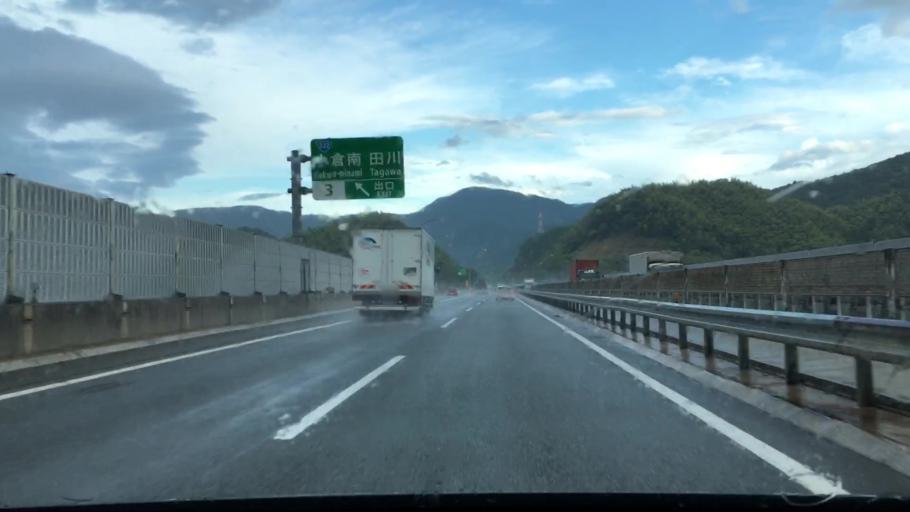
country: JP
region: Fukuoka
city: Kitakyushu
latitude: 33.8054
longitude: 130.8491
